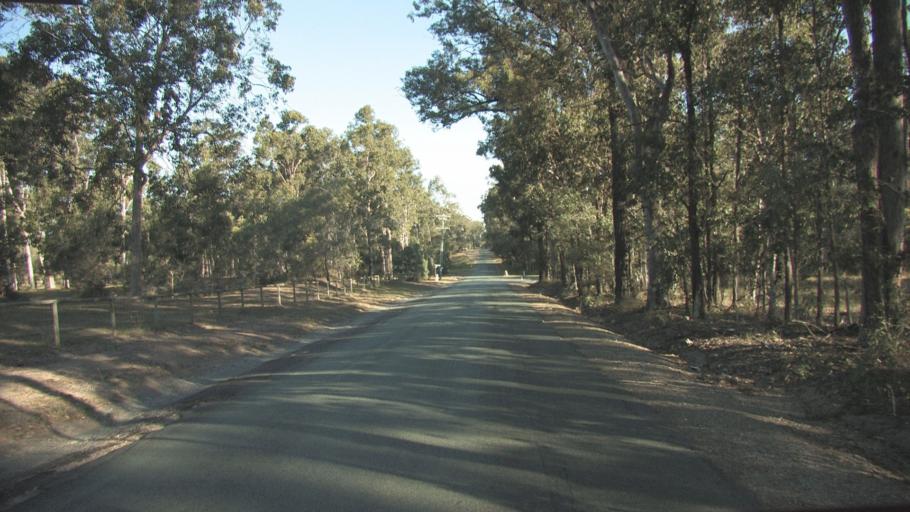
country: AU
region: Queensland
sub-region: Ipswich
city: Springfield Lakes
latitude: -27.7047
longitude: 152.9477
